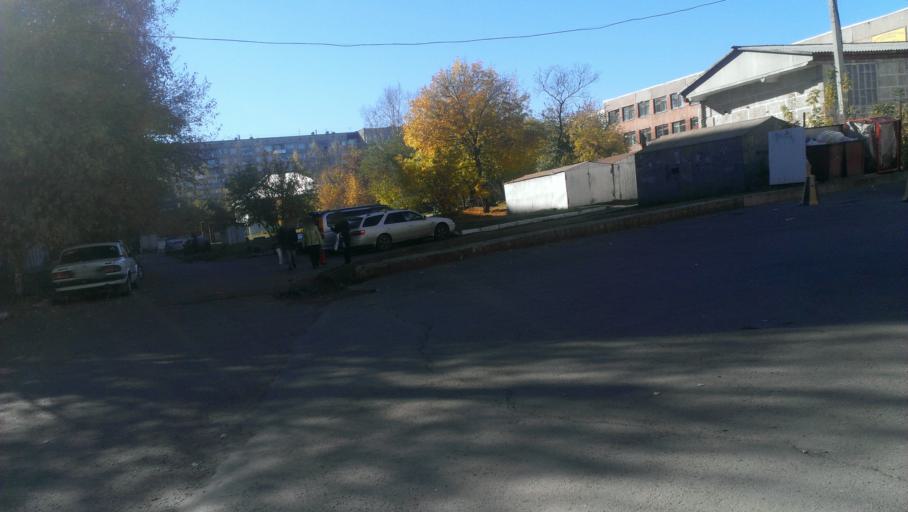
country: RU
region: Altai Krai
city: Novosilikatnyy
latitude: 53.3664
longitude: 83.6676
